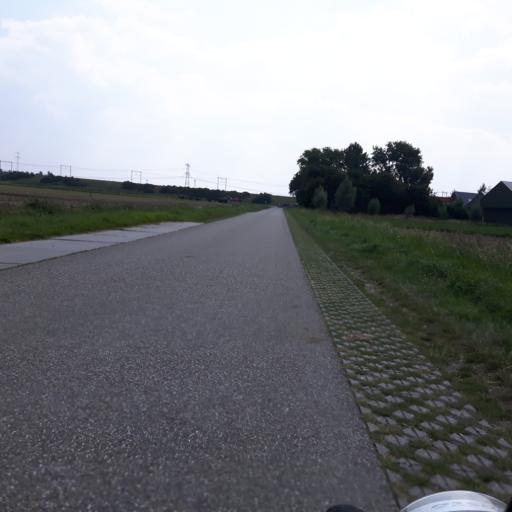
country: NL
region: Zeeland
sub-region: Gemeente Reimerswaal
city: Yerseke
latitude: 51.4736
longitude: 3.9875
